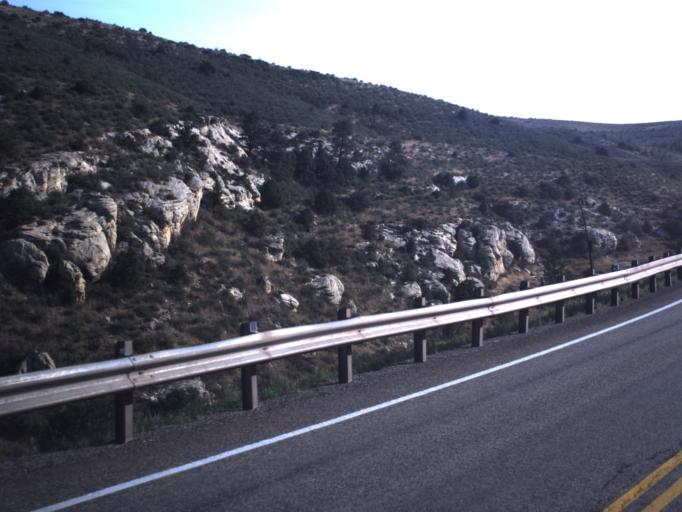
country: US
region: Utah
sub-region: Uintah County
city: Vernal
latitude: 40.6600
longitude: -109.4840
